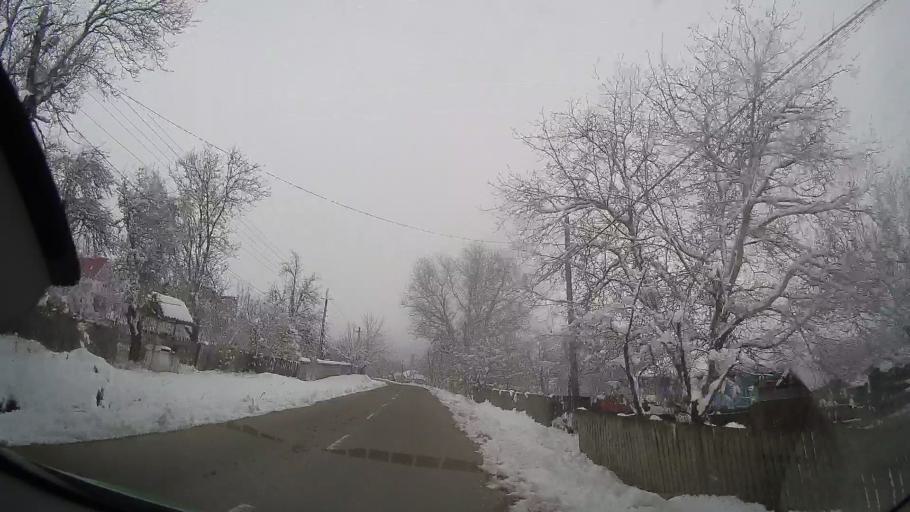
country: RO
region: Neamt
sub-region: Comuna Bozieni
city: Bozieni
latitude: 46.8409
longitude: 27.1475
